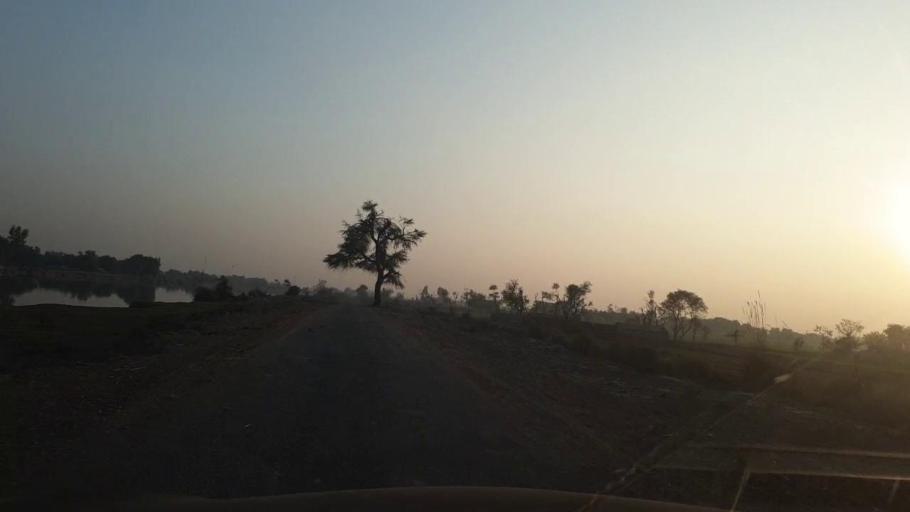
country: PK
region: Sindh
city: Ubauro
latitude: 28.2699
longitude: 69.7798
